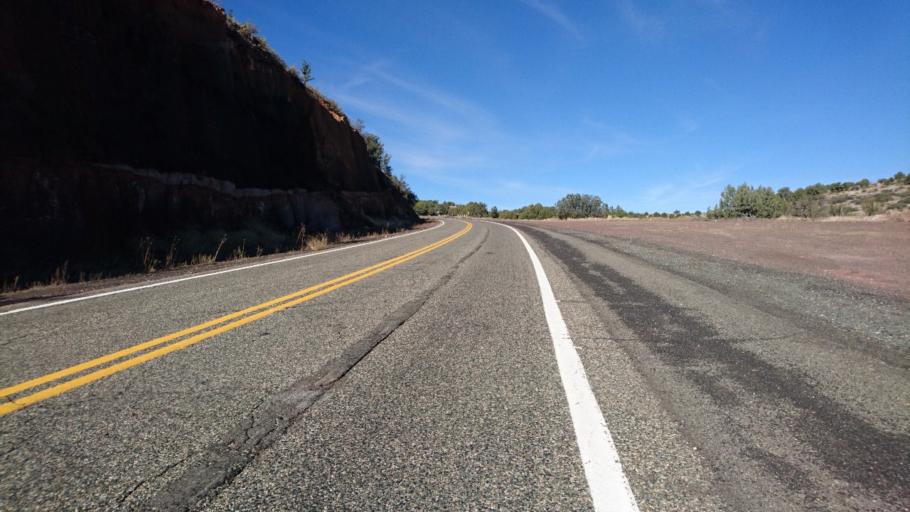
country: US
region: Arizona
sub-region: Yavapai County
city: Paulden
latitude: 35.2774
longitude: -112.6923
